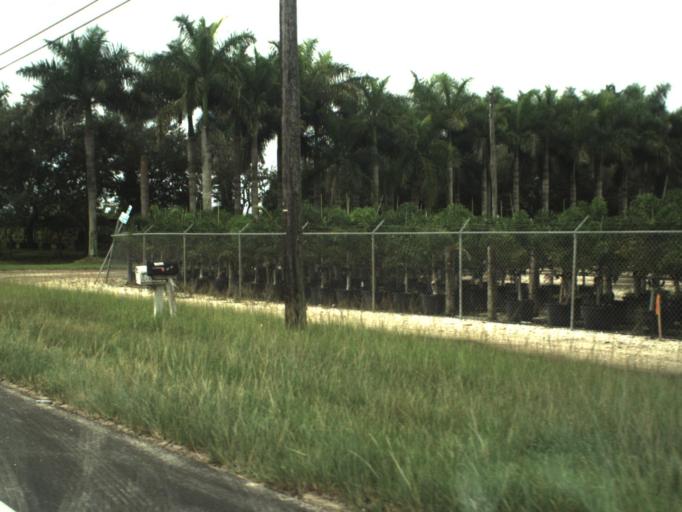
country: US
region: Florida
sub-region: Miami-Dade County
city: Richmond West
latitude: 25.5728
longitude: -80.4783
